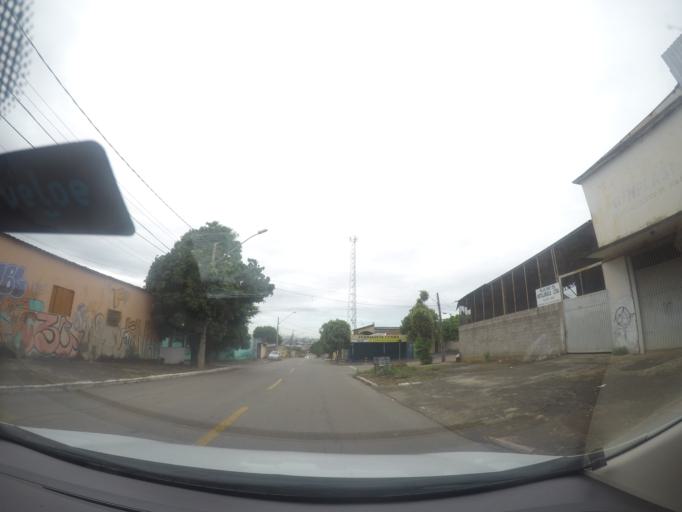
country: BR
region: Goias
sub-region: Goiania
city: Goiania
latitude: -16.6521
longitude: -49.3167
